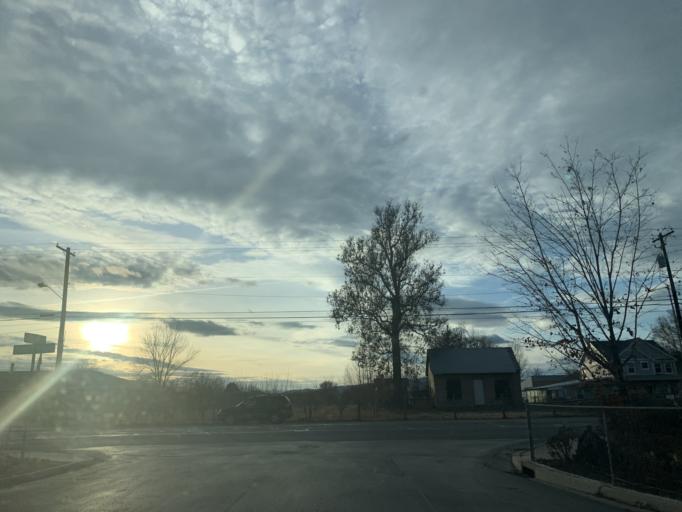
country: US
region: Utah
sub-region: Utah County
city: Provo
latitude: 40.2235
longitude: -111.6774
